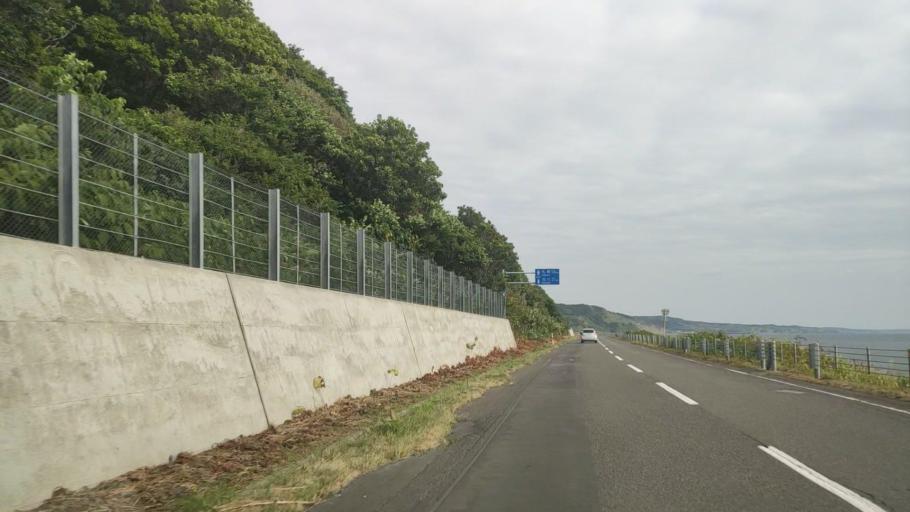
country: JP
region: Hokkaido
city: Ishikari
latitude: 43.4313
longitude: 141.4205
